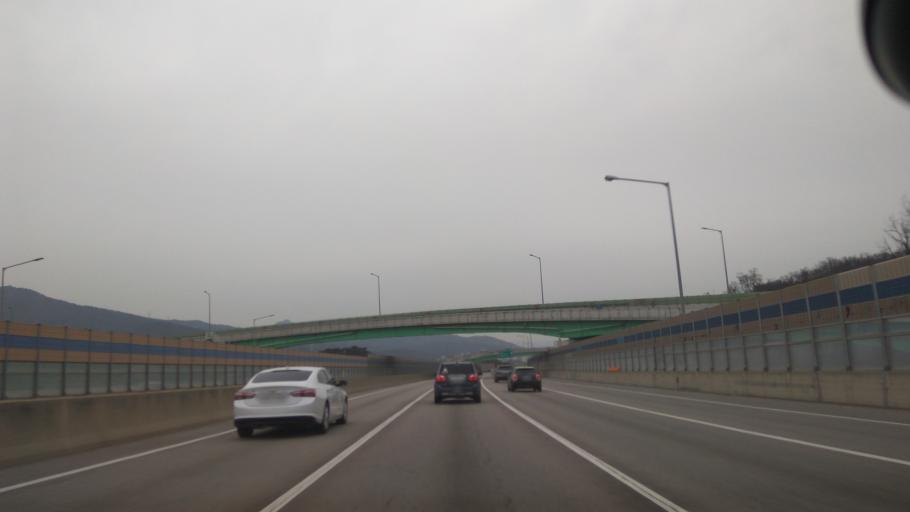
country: KR
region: Gyeonggi-do
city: Uijeongbu-si
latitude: 37.7075
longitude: 127.0406
